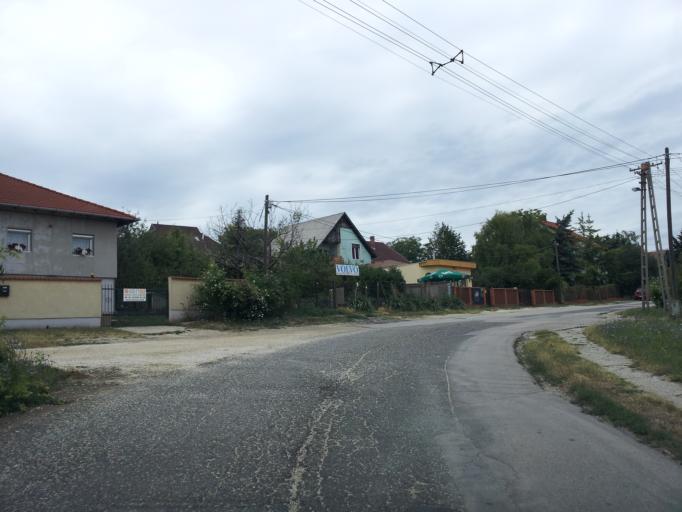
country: HU
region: Pest
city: Erd
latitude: 47.4111
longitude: 18.8763
